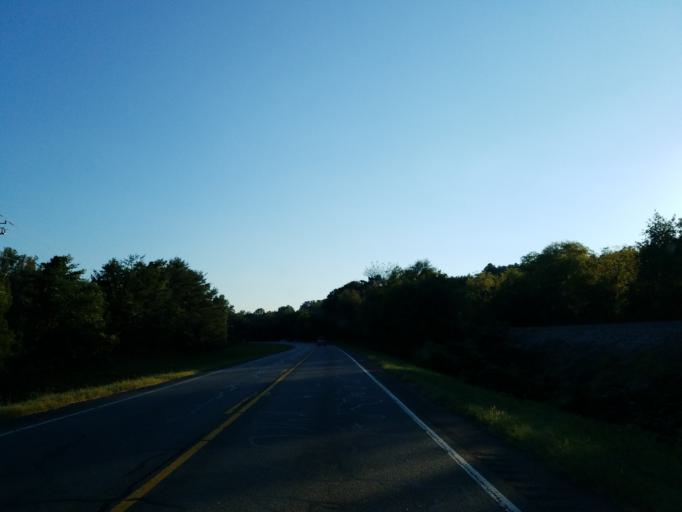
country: US
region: Georgia
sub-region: Bartow County
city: Rydal
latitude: 34.3555
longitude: -84.7206
